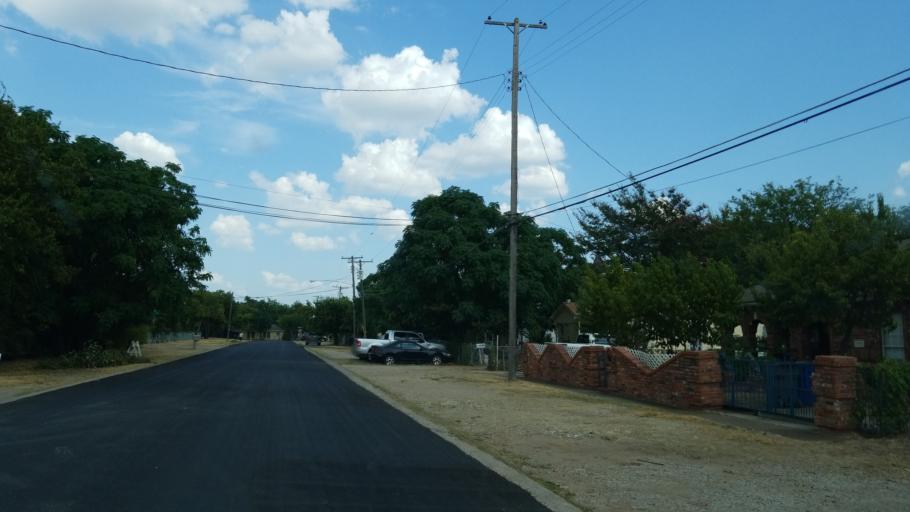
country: US
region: Texas
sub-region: Dallas County
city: Dallas
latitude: 32.7704
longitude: -96.8412
